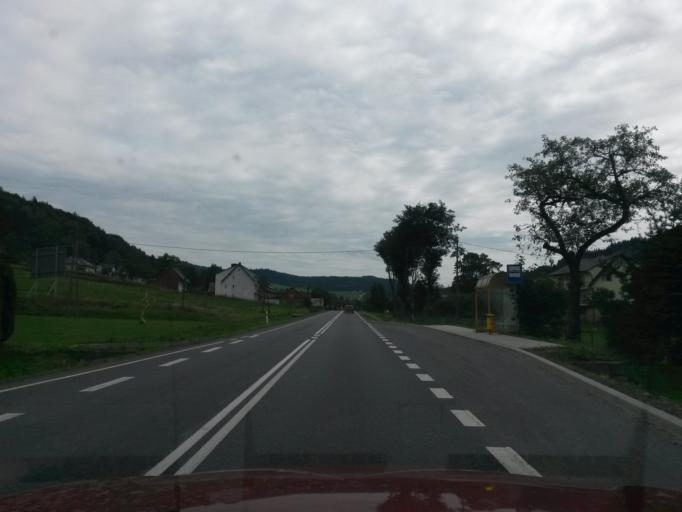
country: PL
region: Lesser Poland Voivodeship
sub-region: Powiat nowosadecki
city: Labowa
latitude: 49.5047
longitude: 20.8950
